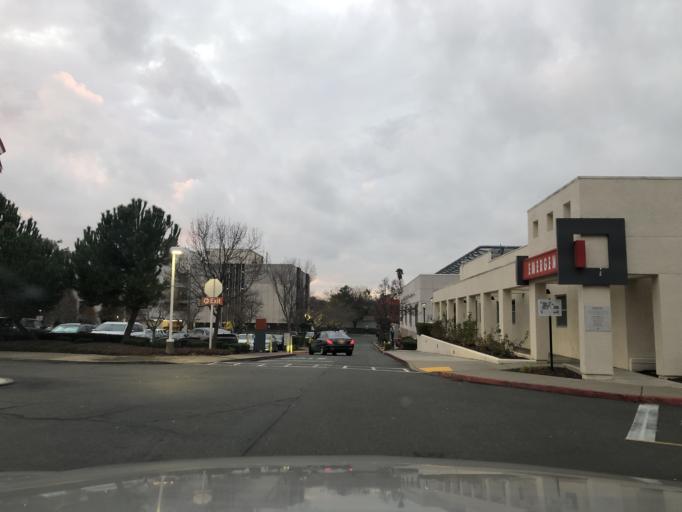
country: US
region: California
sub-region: Sacramento County
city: Foothill Farms
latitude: 38.6690
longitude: -121.3133
